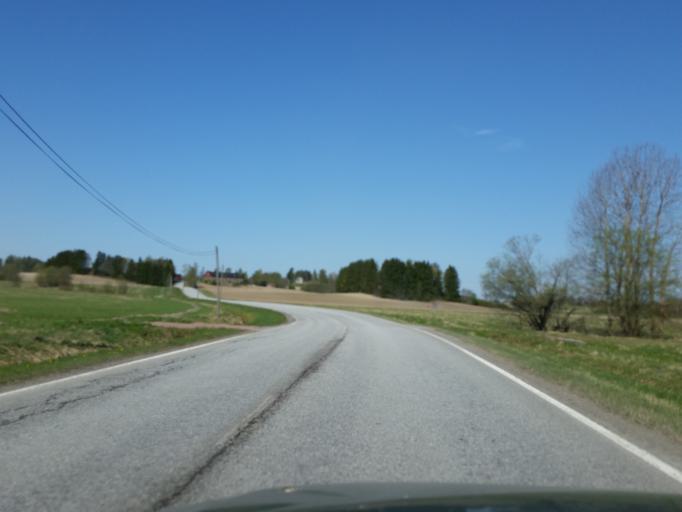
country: FI
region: Uusimaa
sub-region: Helsinki
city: Siuntio
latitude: 60.1751
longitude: 24.1562
